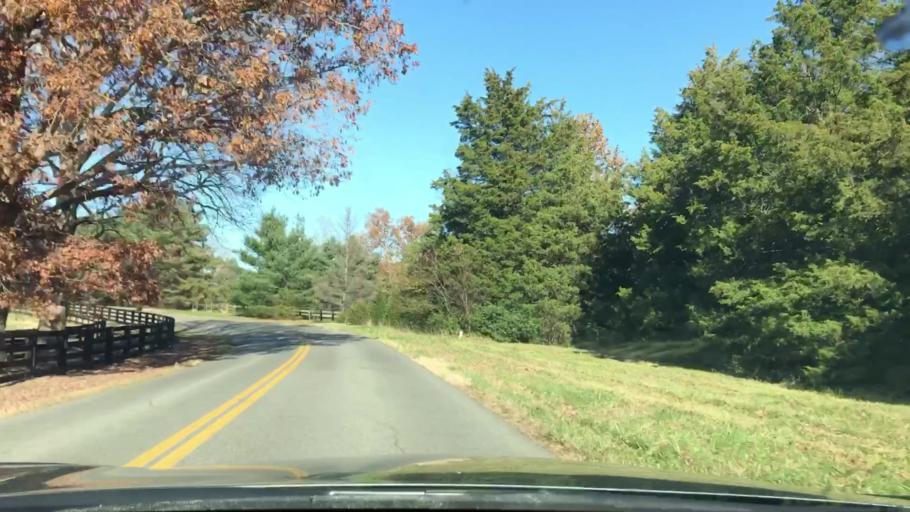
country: US
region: Virginia
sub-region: Henrico County
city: Short Pump
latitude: 37.6573
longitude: -77.7168
